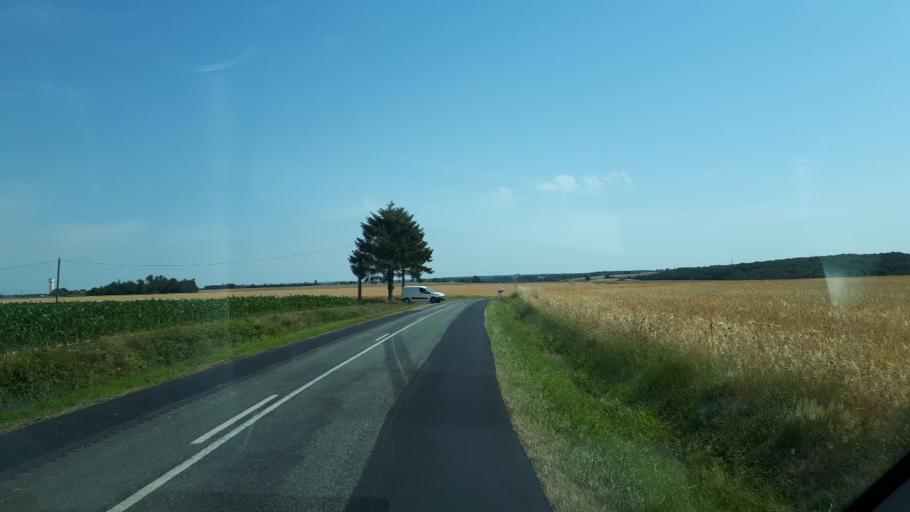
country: FR
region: Centre
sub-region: Departement du Loir-et-Cher
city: Aze
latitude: 47.8772
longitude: 1.0099
